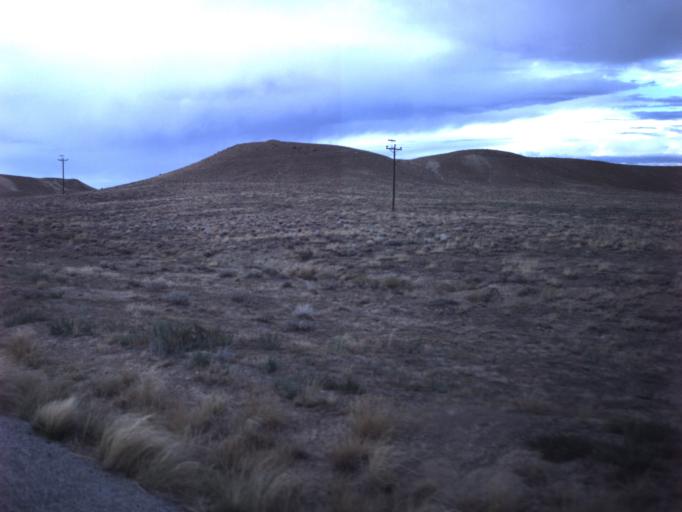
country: US
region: Utah
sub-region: Grand County
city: Moab
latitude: 38.9267
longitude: -109.3400
